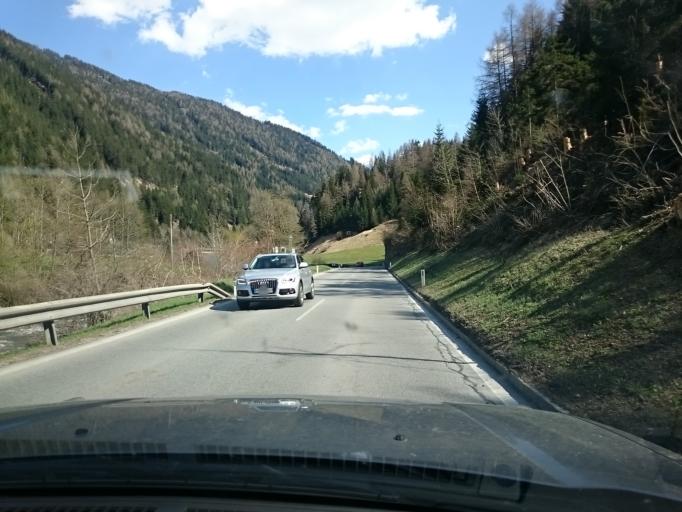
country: AT
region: Tyrol
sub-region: Politischer Bezirk Innsbruck Land
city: Steinach am Brenner
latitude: 47.0800
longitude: 11.4758
